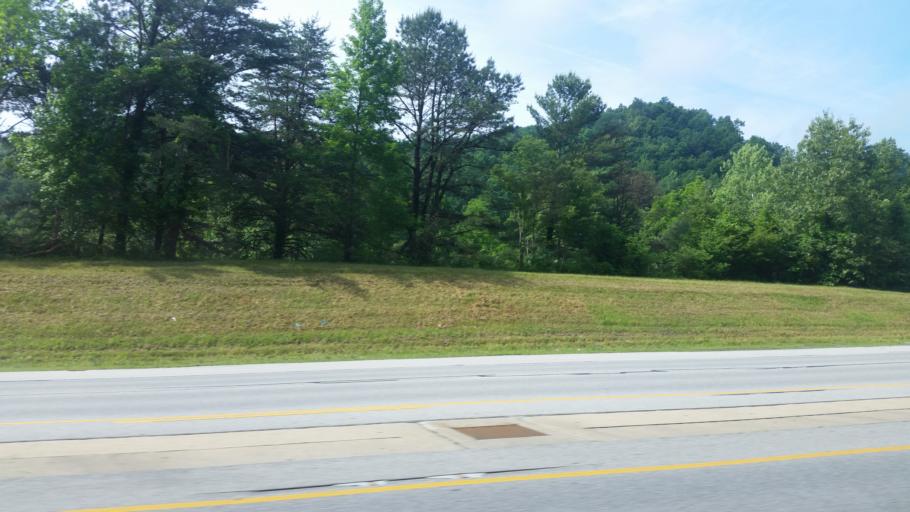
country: US
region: Kentucky
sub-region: Rowan County
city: Morehead
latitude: 38.1808
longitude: -83.4477
